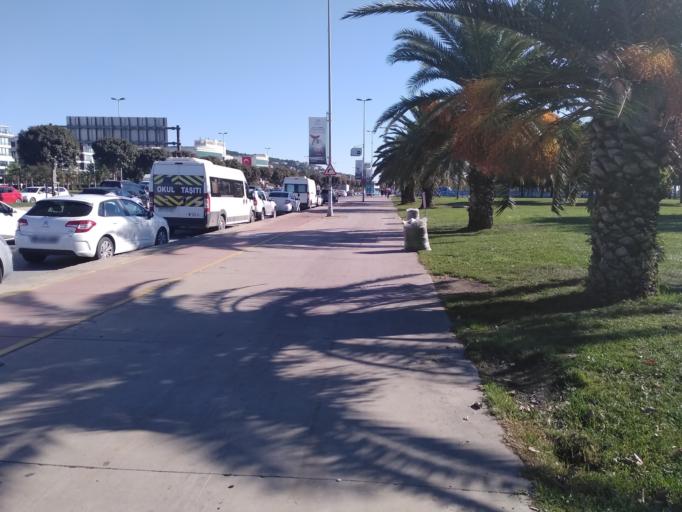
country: TR
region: Istanbul
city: Maltepe
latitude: 40.9167
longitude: 29.1310
